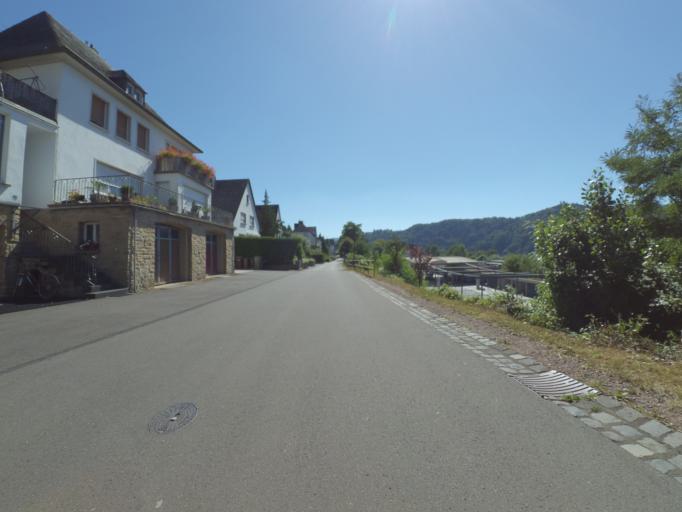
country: DE
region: Rheinland-Pfalz
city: Bullay
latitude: 50.0553
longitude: 7.1353
